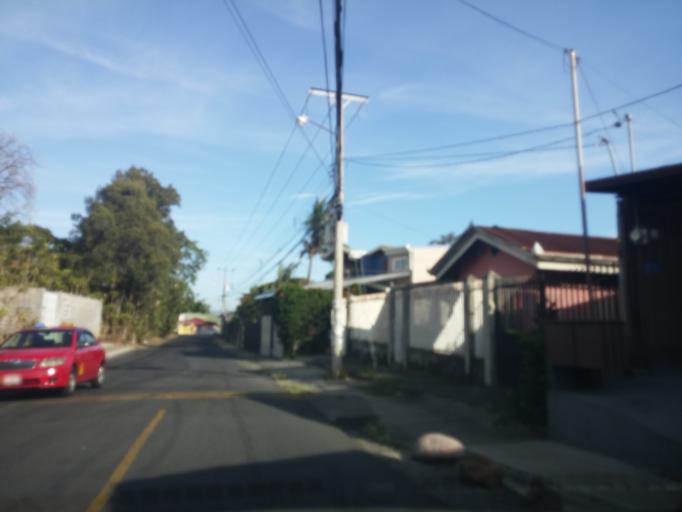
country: CR
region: Heredia
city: Mercedes
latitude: 10.0001
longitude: -84.1361
